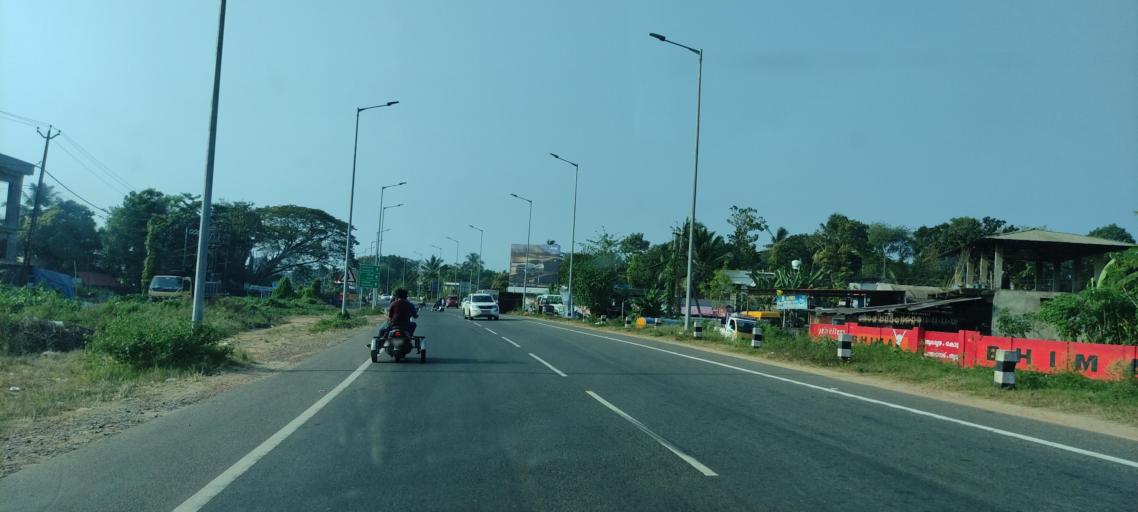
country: IN
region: Kerala
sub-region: Alappuzha
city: Alleppey
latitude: 9.4698
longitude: 76.3373
